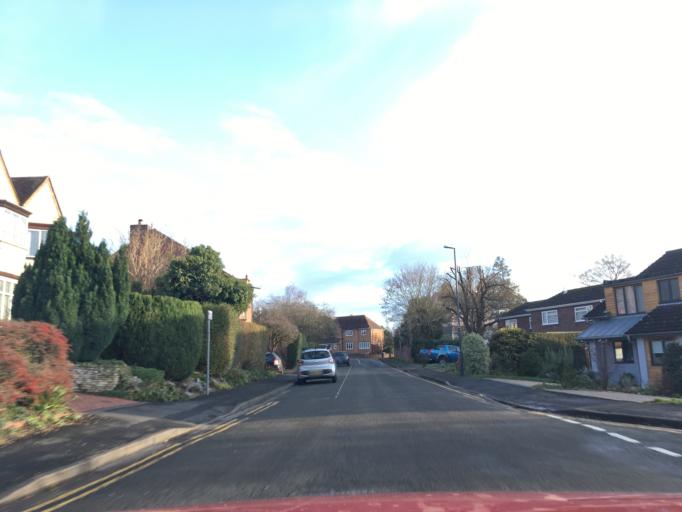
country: GB
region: England
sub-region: Warwickshire
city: Stratford-upon-Avon
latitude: 52.2010
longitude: -1.7047
